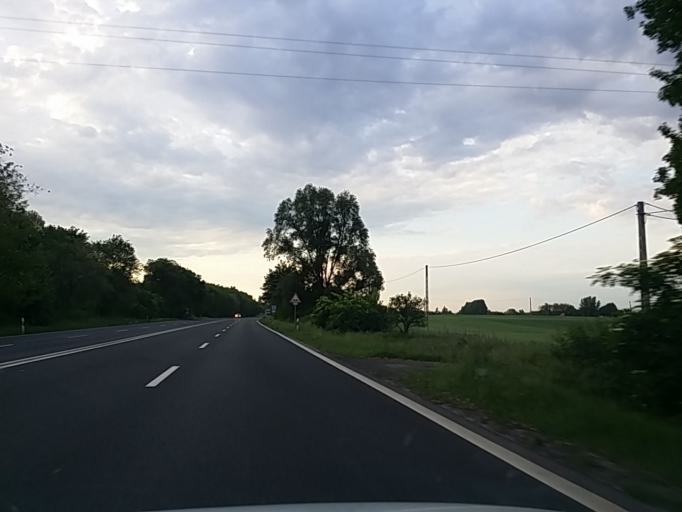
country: HU
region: Bacs-Kiskun
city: Lajosmizse
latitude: 46.9716
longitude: 19.6325
